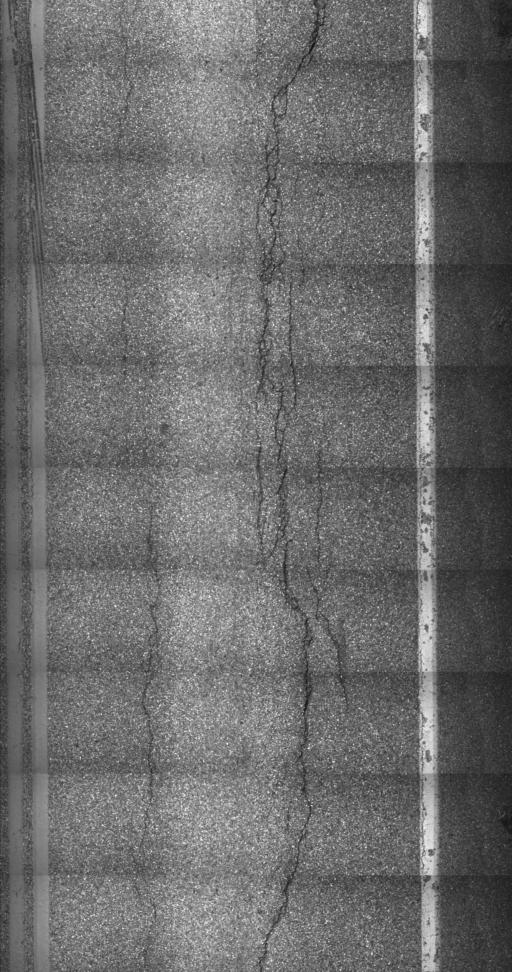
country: US
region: Vermont
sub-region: Bennington County
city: Manchester Center
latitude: 43.2620
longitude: -73.1046
